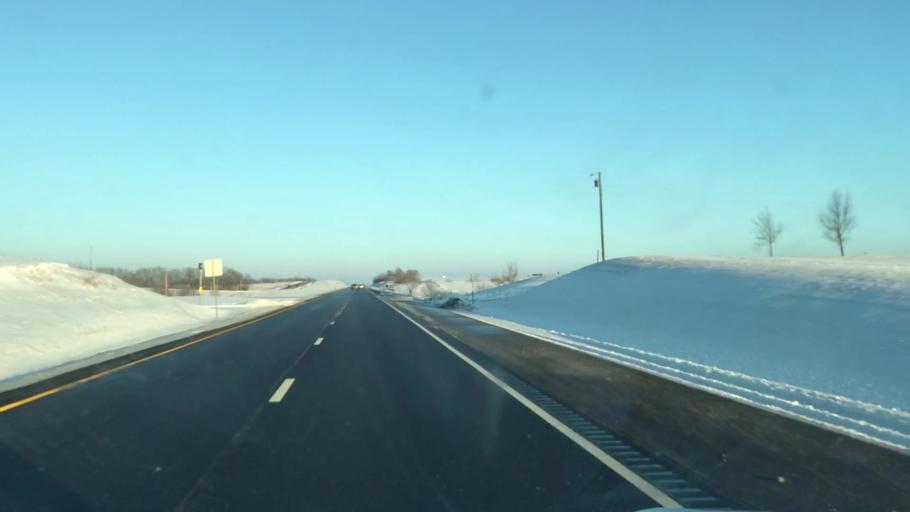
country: US
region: Missouri
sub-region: Clinton County
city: Gower
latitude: 39.7617
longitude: -94.5378
